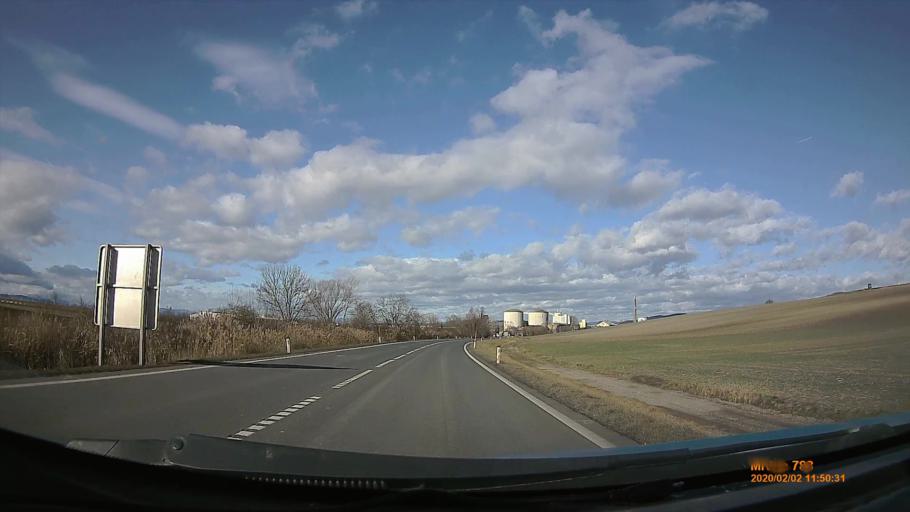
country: AT
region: Burgenland
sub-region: Eisenstadt-Umgebung
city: Klingenbach
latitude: 47.7628
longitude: 16.5385
